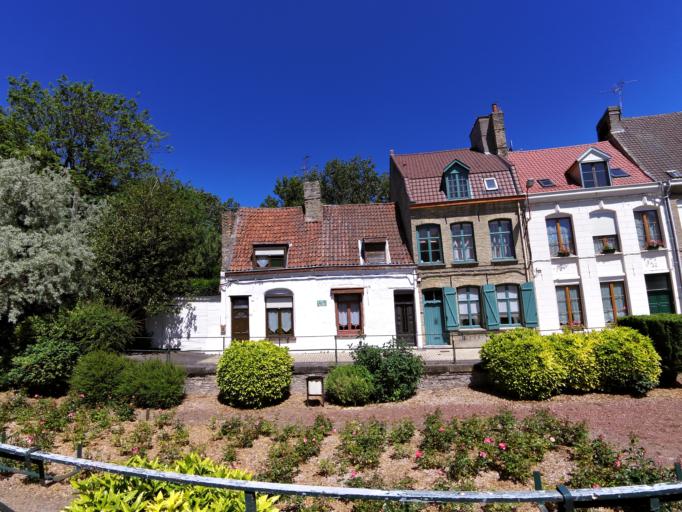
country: FR
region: Nord-Pas-de-Calais
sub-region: Departement du Nord
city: Bergues
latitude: 50.9707
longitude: 2.4337
